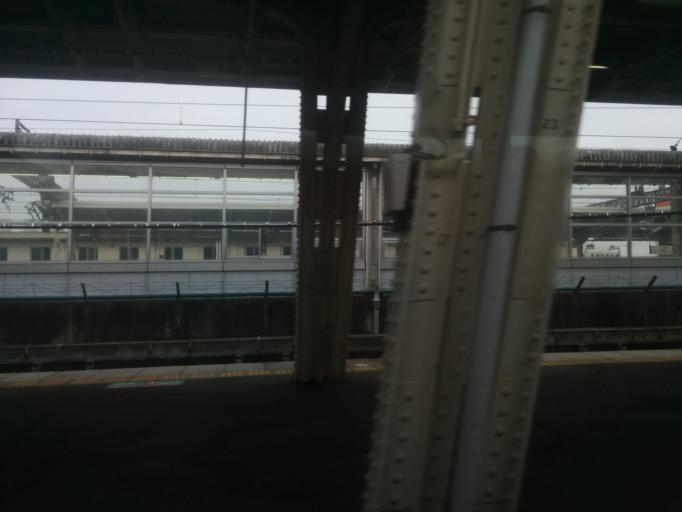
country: JP
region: Shiga Prefecture
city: Nagahama
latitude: 35.3133
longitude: 136.2892
